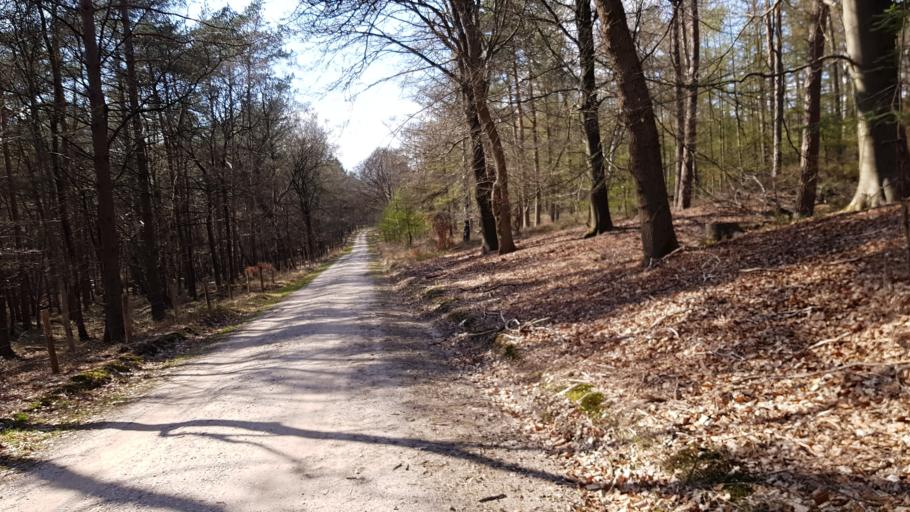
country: NL
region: Gelderland
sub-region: Gemeente Apeldoorn
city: Loenen
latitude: 52.0812
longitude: 5.9655
